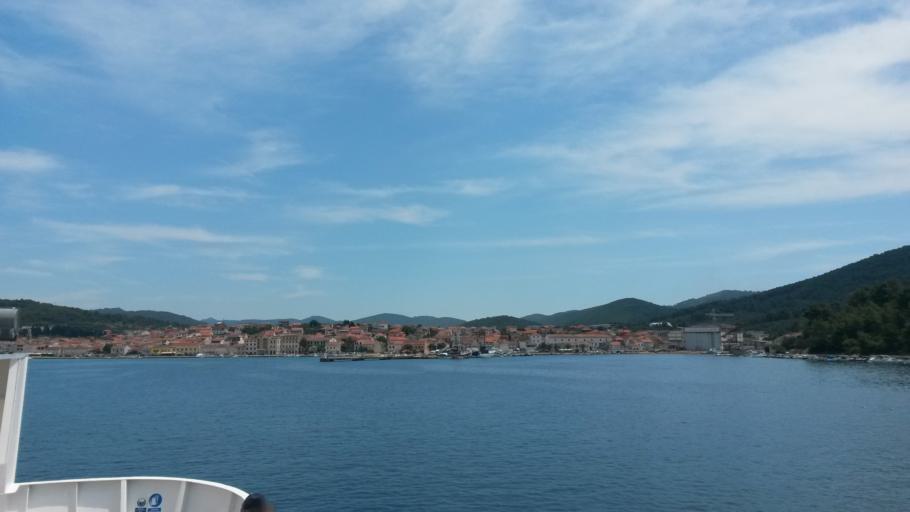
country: HR
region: Dubrovacko-Neretvanska
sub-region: Grad Dubrovnik
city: Vela Luka
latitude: 42.9609
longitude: 16.7058
